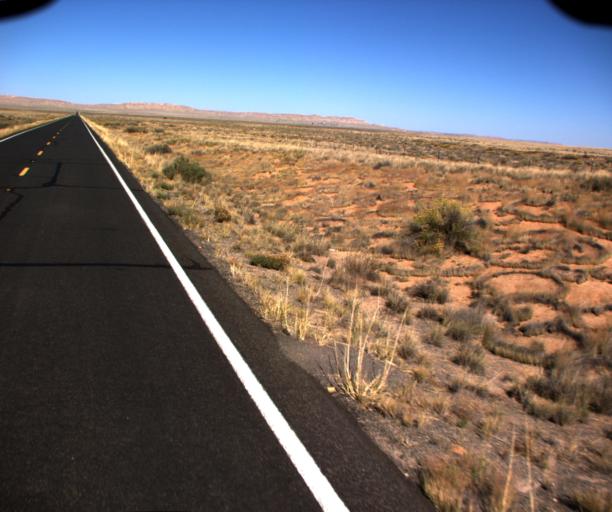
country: US
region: Arizona
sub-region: Navajo County
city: First Mesa
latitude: 35.6991
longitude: -110.5070
